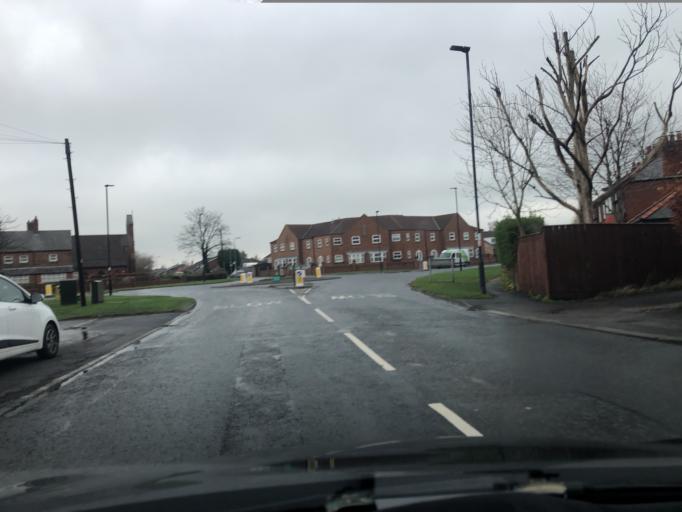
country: GB
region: England
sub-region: North Yorkshire
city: Stokesley
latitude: 54.4742
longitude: -1.1867
